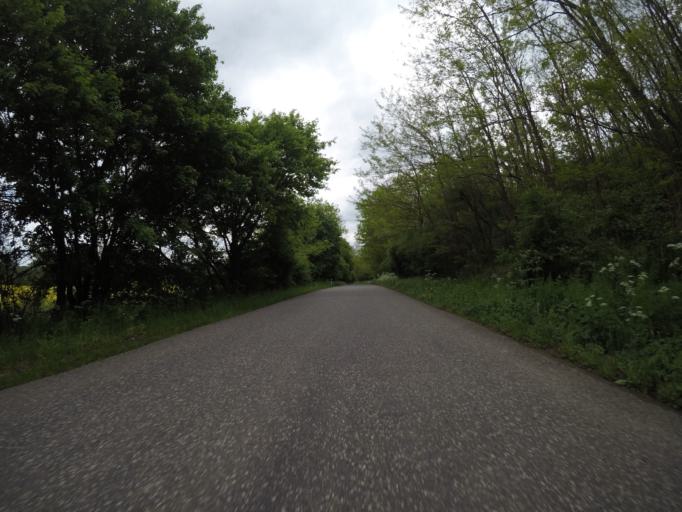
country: SK
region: Banskobystricky
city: Dudince
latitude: 48.0951
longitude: 18.8711
